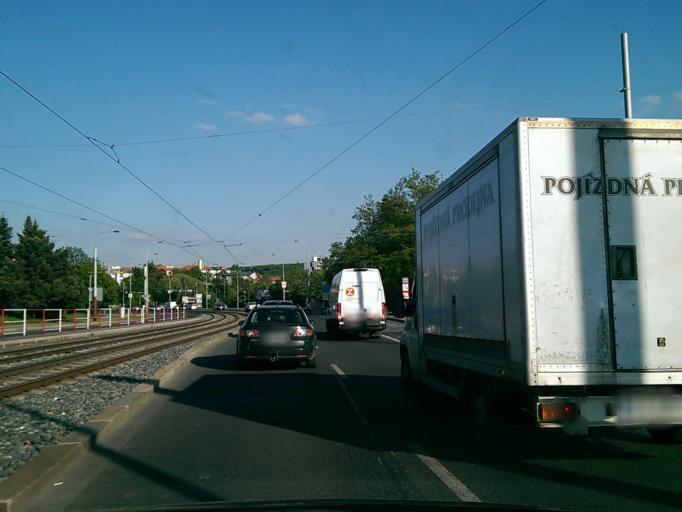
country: CZ
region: Praha
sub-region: Praha 14
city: Hostavice
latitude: 50.0537
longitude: 14.5191
